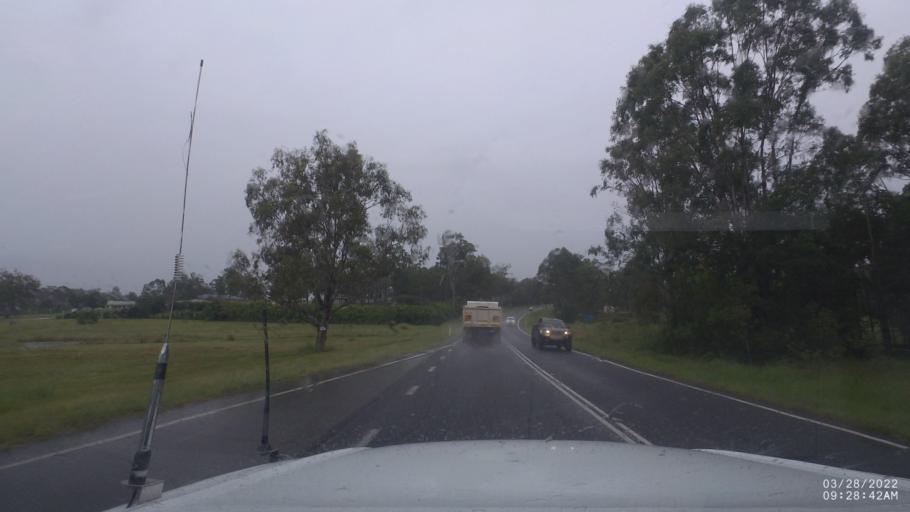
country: AU
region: Queensland
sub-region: Logan
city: Cedar Vale
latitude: -27.8909
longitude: 153.1174
